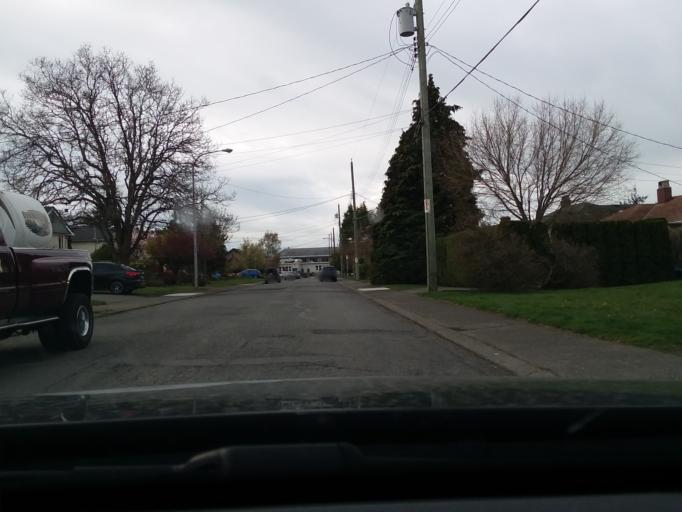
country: CA
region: British Columbia
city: Oak Bay
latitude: 48.4477
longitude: -123.3284
